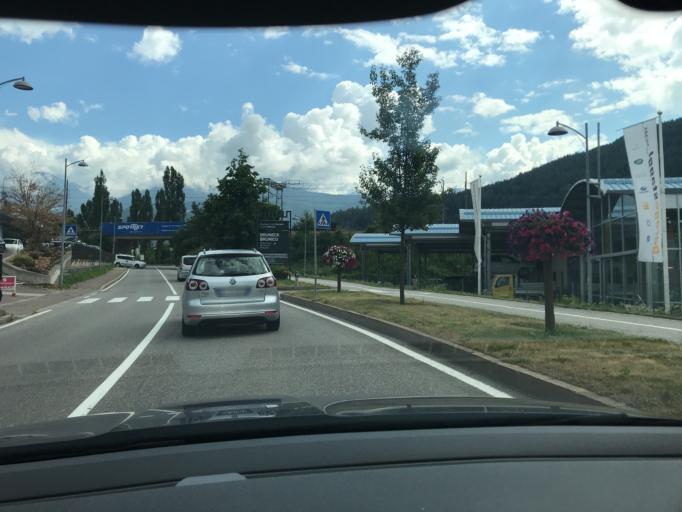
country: IT
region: Trentino-Alto Adige
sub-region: Bolzano
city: Brunico
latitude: 46.7882
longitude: 11.9237
